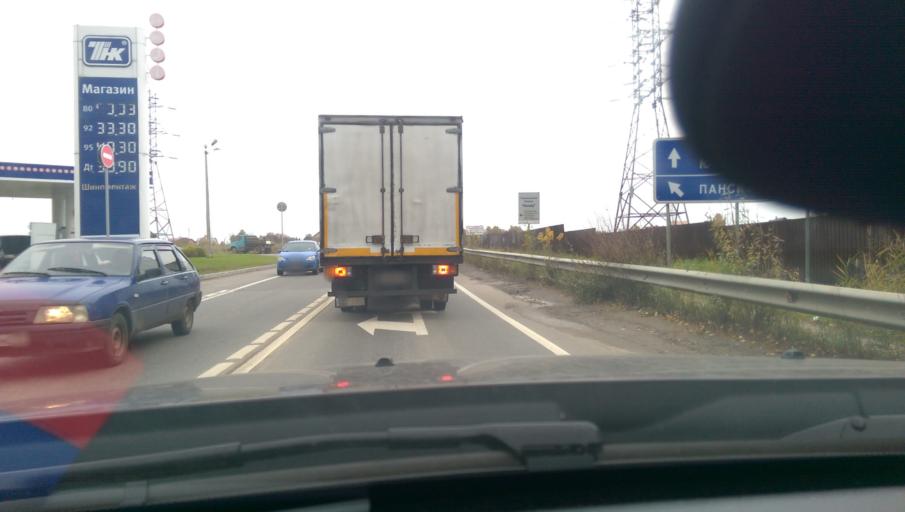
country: RU
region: Moskovskaya
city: Pirogovskiy
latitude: 55.9963
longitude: 37.7275
